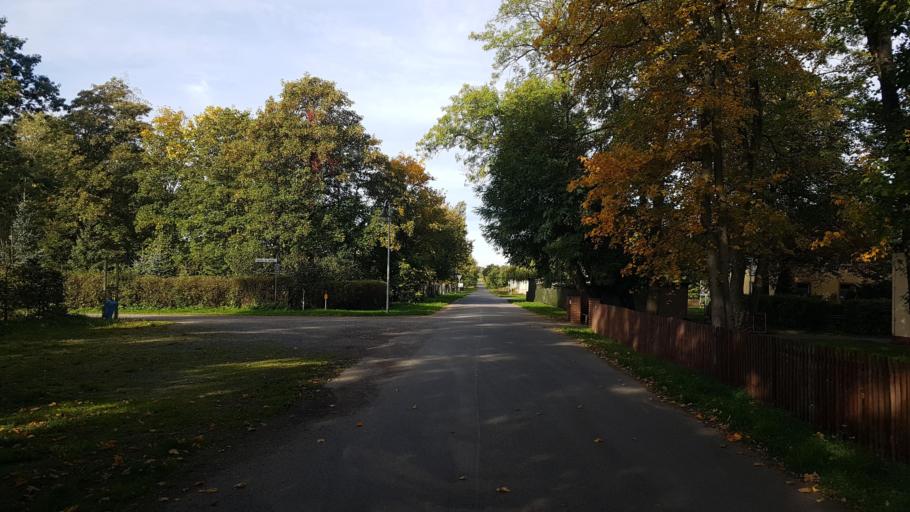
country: DE
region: Brandenburg
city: Drahnsdorf
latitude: 51.8483
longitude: 13.5251
